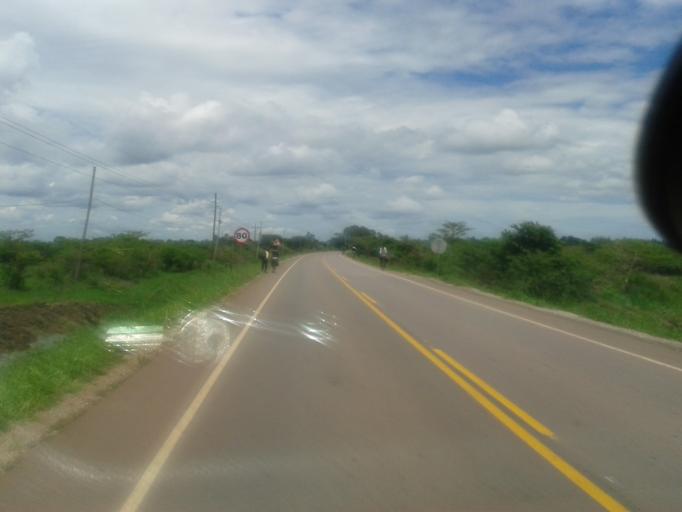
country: UG
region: Western Region
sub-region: Kiryandongo District
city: Kiryandongo
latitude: 1.7857
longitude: 32.0162
